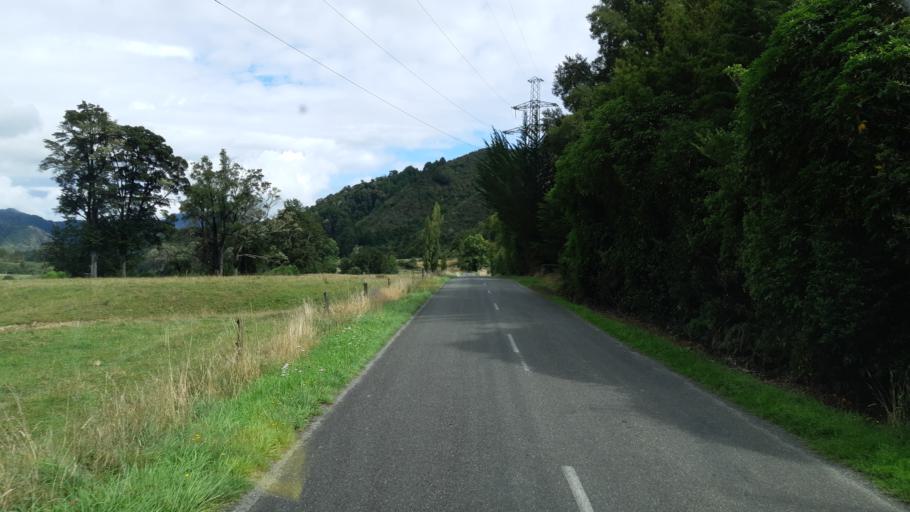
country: NZ
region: West Coast
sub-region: Buller District
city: Westport
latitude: -41.7886
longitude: 172.3601
